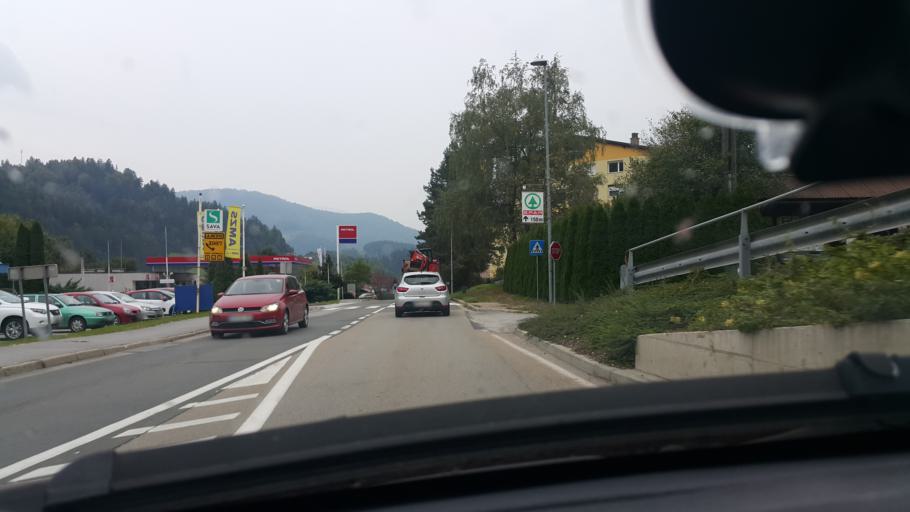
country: SI
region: Dravograd
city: Dravograd
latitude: 46.5919
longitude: 15.0299
